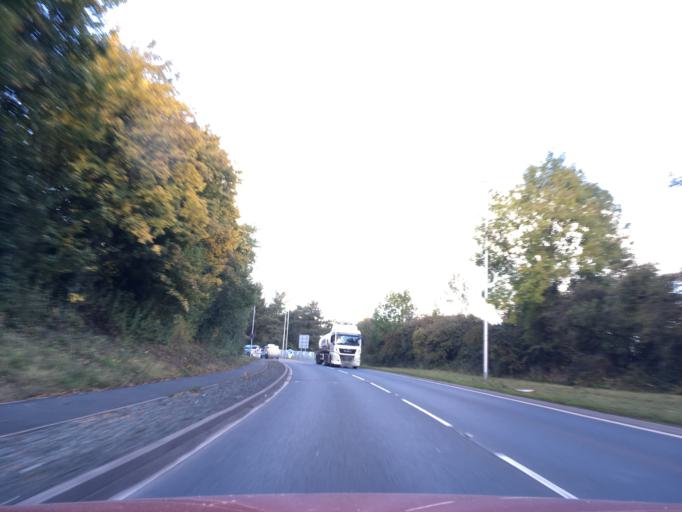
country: GB
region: Wales
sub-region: Sir Powys
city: Brecon
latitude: 51.9442
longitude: -3.4108
